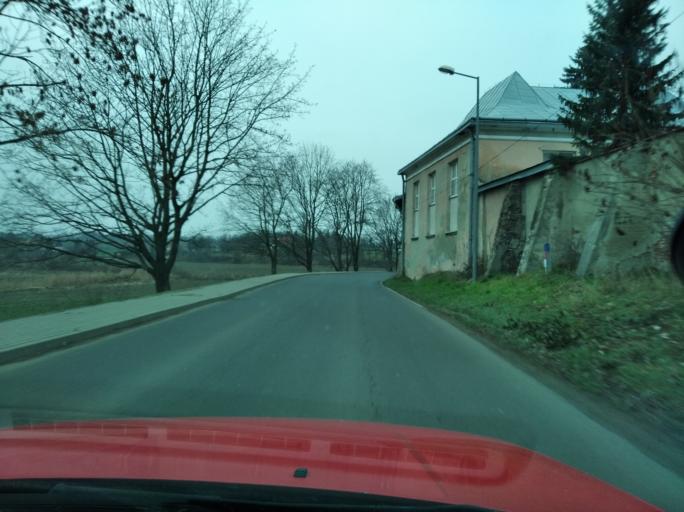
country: PL
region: Subcarpathian Voivodeship
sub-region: Powiat jaroslawski
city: Pawlosiow
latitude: 50.0082
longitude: 22.6548
